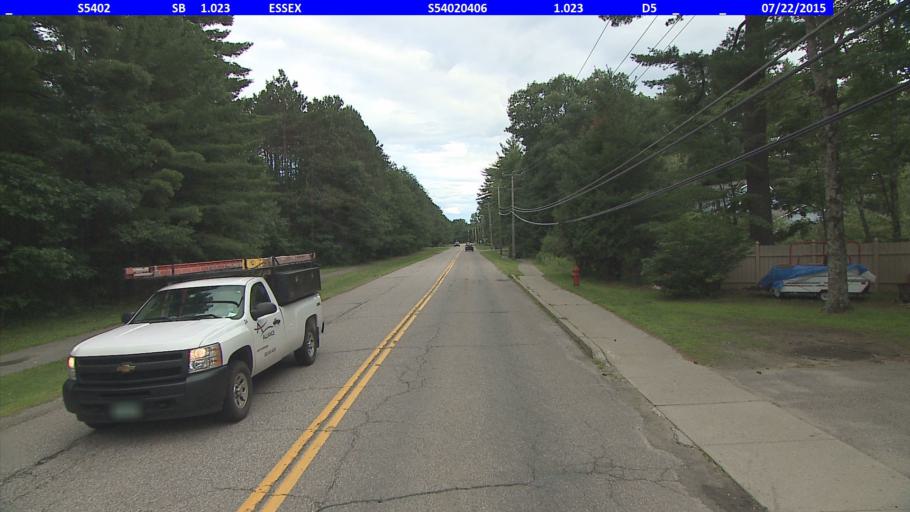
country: US
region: Vermont
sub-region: Chittenden County
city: Jericho
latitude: 44.4932
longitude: -73.0499
